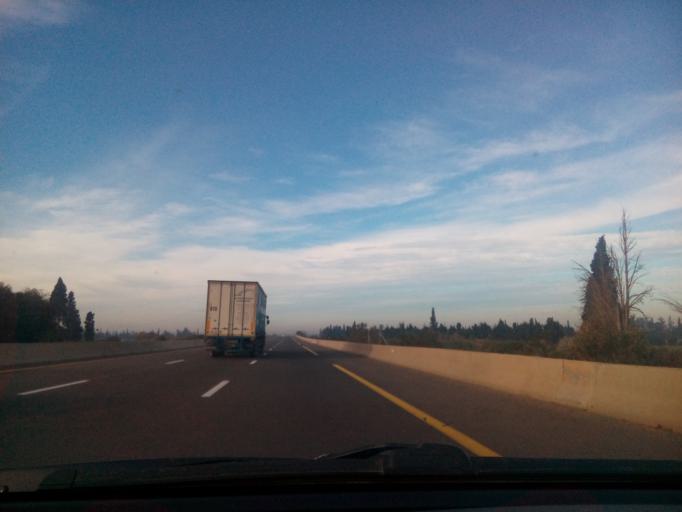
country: DZ
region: Mascara
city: Sig
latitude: 35.6174
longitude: 0.0280
